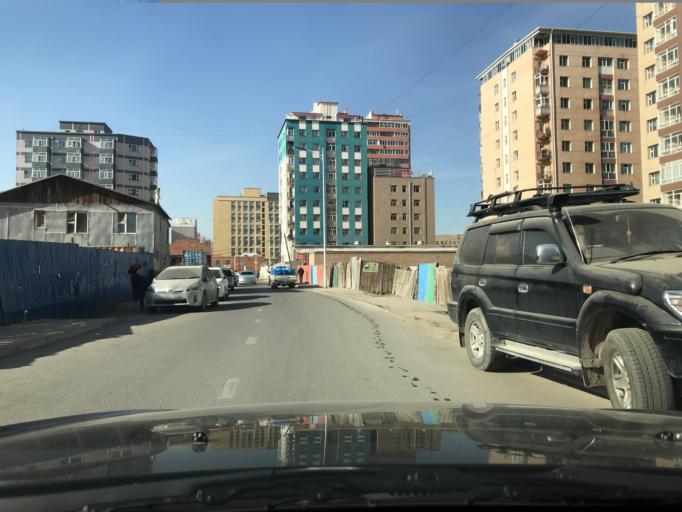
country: MN
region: Ulaanbaatar
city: Ulaanbaatar
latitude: 47.9121
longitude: 106.9525
